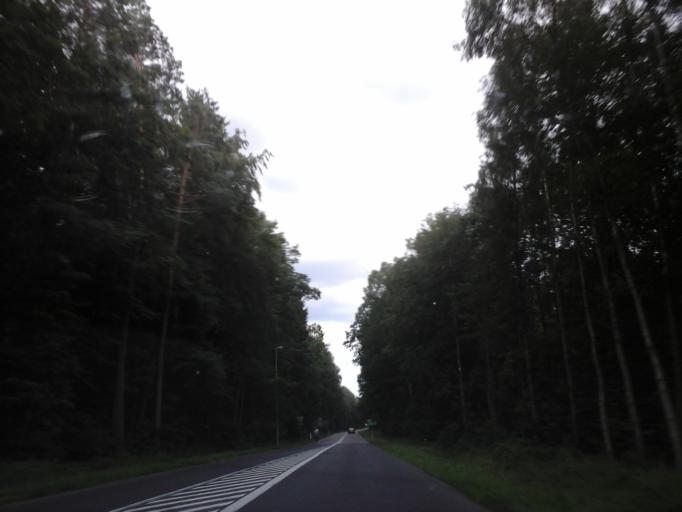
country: PL
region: West Pomeranian Voivodeship
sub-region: Powiat kamienski
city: Golczewo
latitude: 53.8069
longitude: 15.0109
